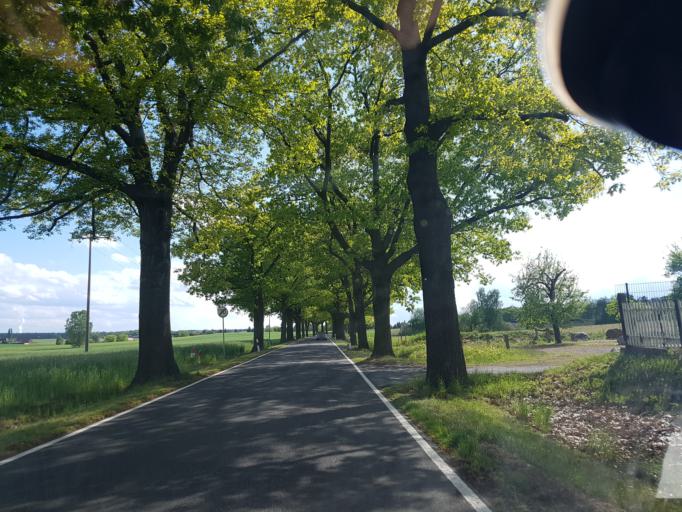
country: DE
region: Brandenburg
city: Spremberg
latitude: 51.6596
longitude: 14.3364
